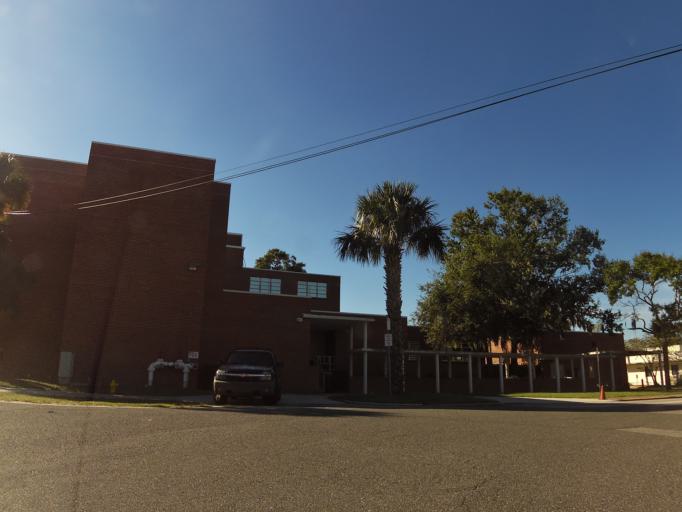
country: US
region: Florida
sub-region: Duval County
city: Jacksonville
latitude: 30.3500
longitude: -81.6626
